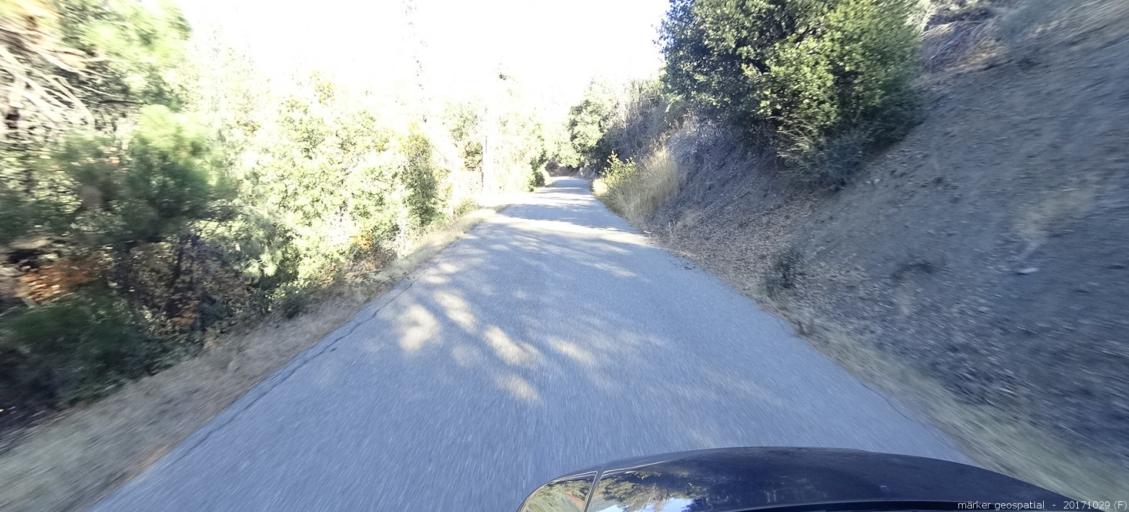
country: US
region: California
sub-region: Trinity County
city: Hayfork
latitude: 40.3778
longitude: -122.9773
